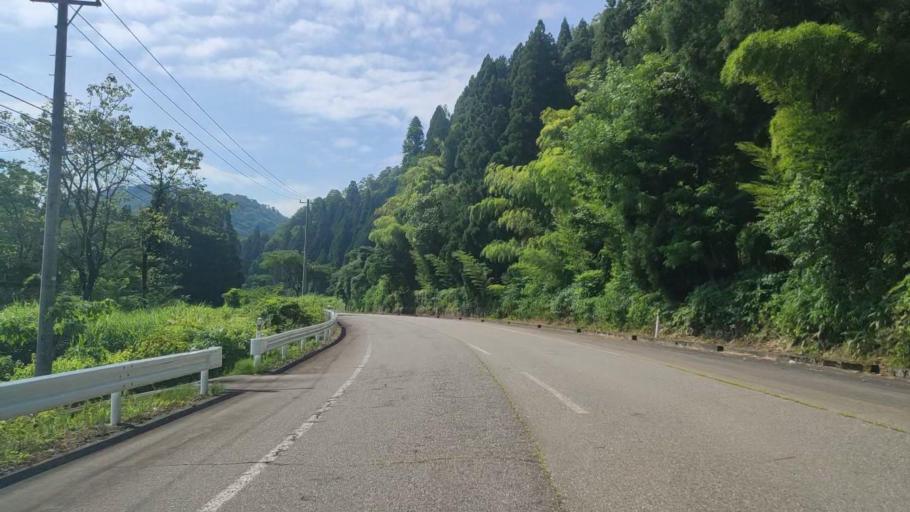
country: JP
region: Ishikawa
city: Komatsu
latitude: 36.3254
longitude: 136.5291
